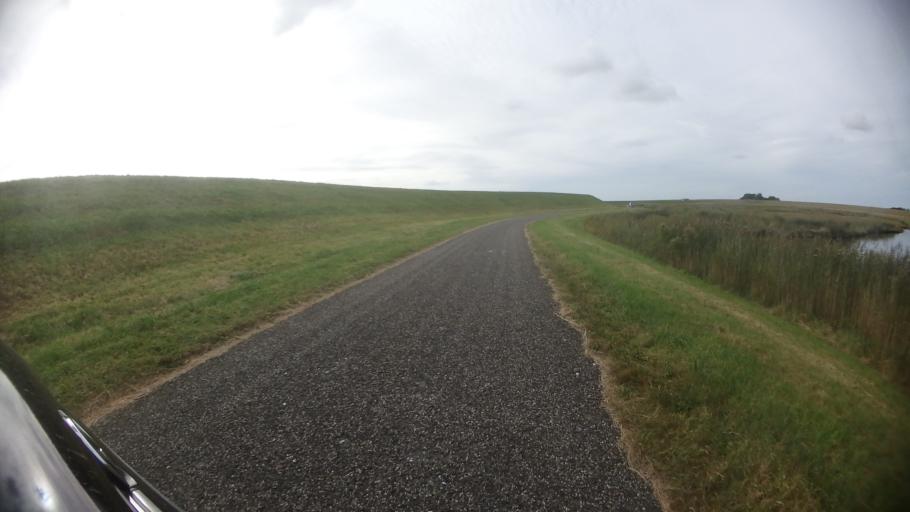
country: NL
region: North Holland
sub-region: Gemeente Texel
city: Den Burg
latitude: 53.0674
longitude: 4.8789
